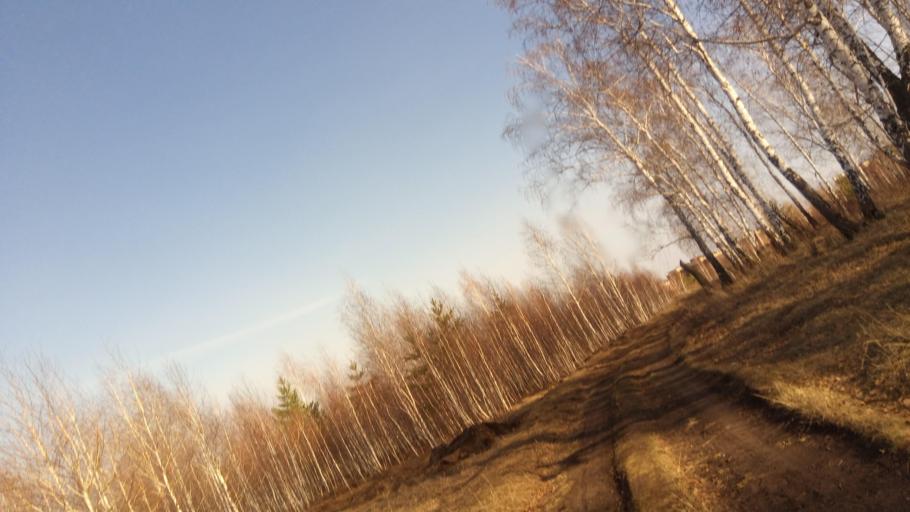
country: RU
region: Chelyabinsk
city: Sargazy
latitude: 55.1141
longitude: 61.2442
